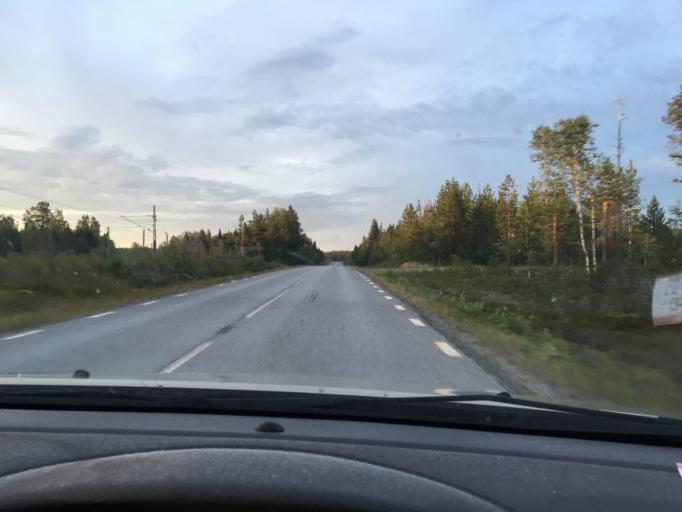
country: SE
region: Norrbotten
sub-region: Lulea Kommun
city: Ranea
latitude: 66.0500
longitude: 22.3586
